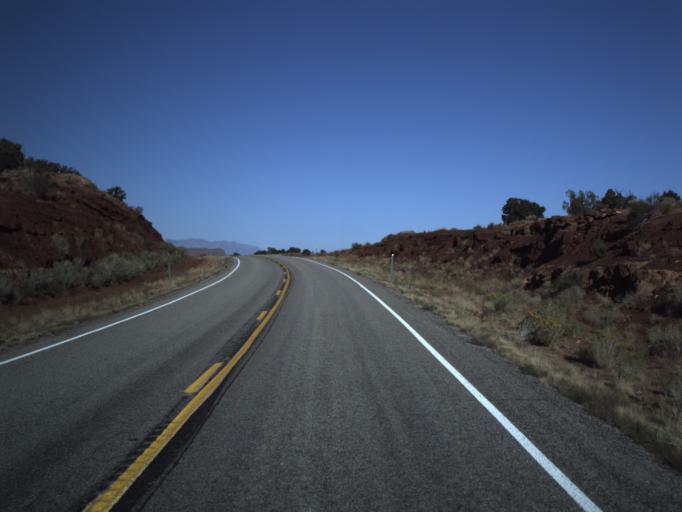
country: US
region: Utah
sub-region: San Juan County
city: Blanding
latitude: 37.6502
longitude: -110.1203
